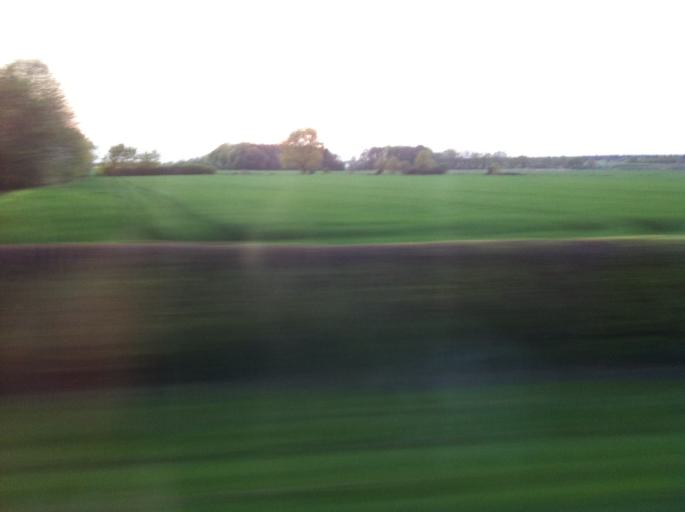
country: DE
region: Schleswig-Holstein
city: Wohltorf
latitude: 53.5395
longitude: 10.2713
